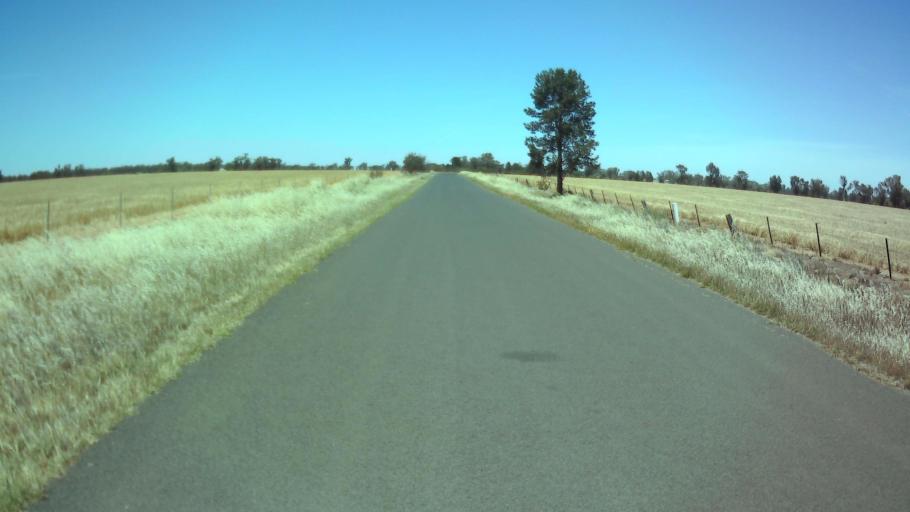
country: AU
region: New South Wales
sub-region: Weddin
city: Grenfell
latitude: -34.0526
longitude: 147.7813
